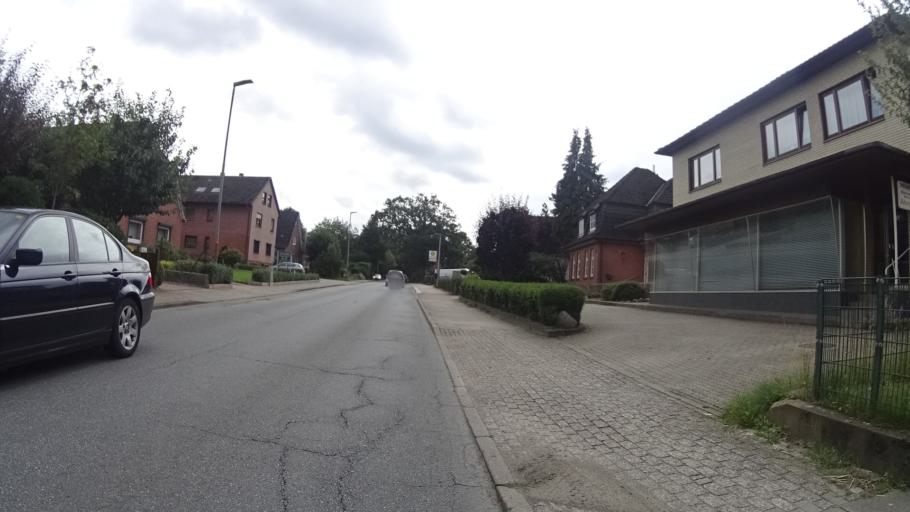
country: DE
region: Schleswig-Holstein
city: Tangstedt
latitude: 53.7438
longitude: 10.0682
